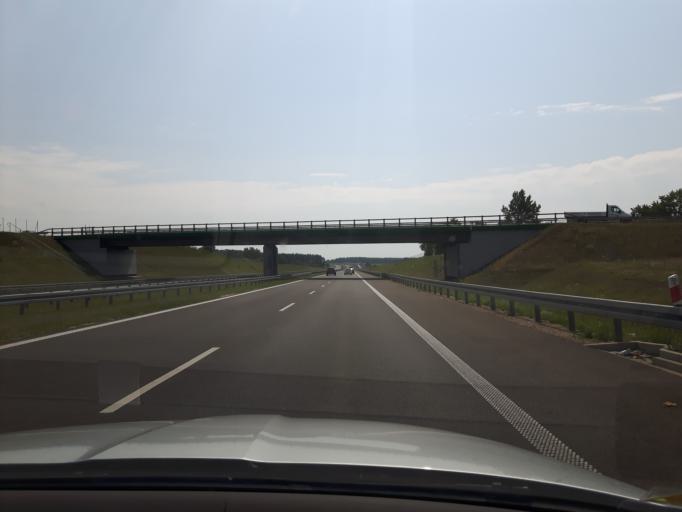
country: PL
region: Warmian-Masurian Voivodeship
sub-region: Powiat nidzicki
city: Nidzica
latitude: 53.3133
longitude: 20.4378
